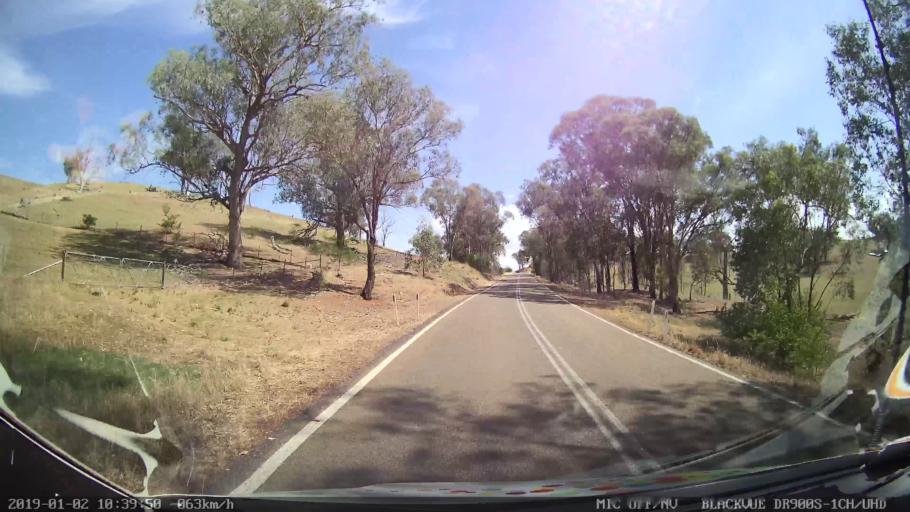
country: AU
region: New South Wales
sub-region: Gundagai
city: Gundagai
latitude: -34.8074
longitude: 148.3177
